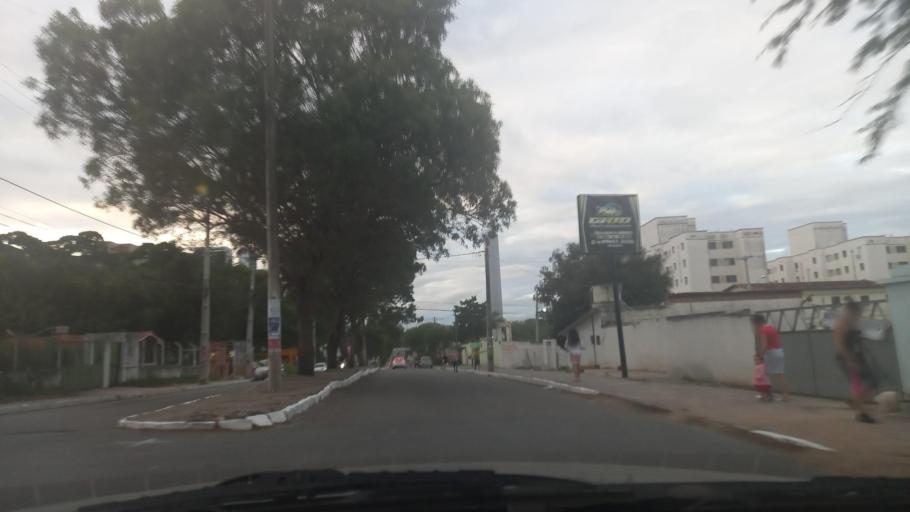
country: BR
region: Pernambuco
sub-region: Caruaru
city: Caruaru
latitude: -8.2631
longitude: -35.9645
